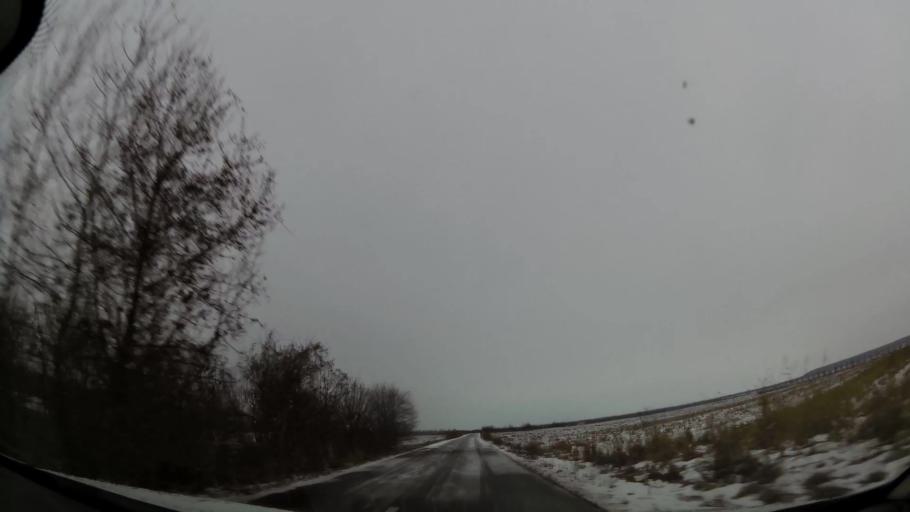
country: RO
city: Fantanele
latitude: 44.7341
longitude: 25.9006
